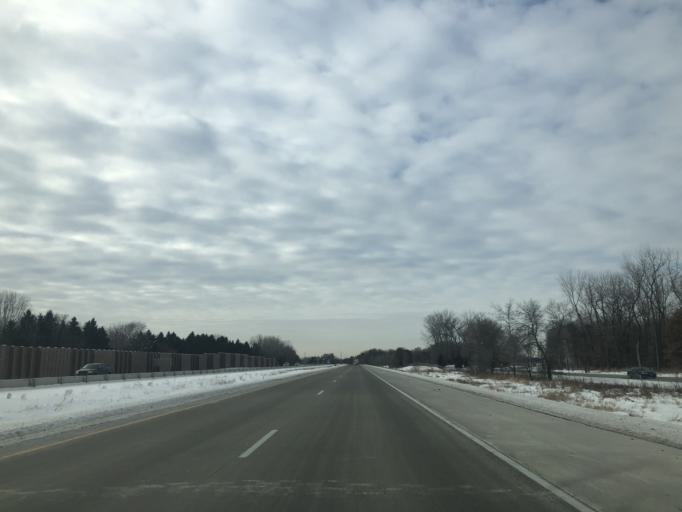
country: US
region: Minnesota
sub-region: Anoka County
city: Circle Pines
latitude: 45.1677
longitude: -93.1455
